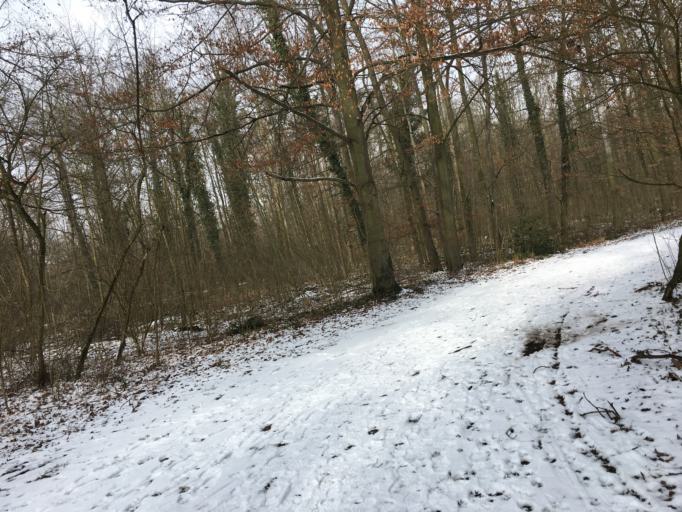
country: DE
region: North Rhine-Westphalia
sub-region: Regierungsbezirk Koln
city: Kreuzau
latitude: 50.7724
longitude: 6.4967
